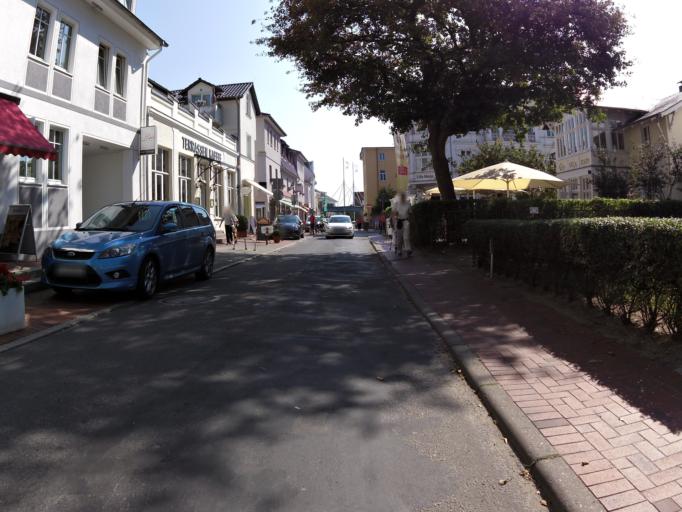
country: DE
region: Mecklenburg-Vorpommern
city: Seebad Heringsdorf
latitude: 53.9579
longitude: 14.1655
